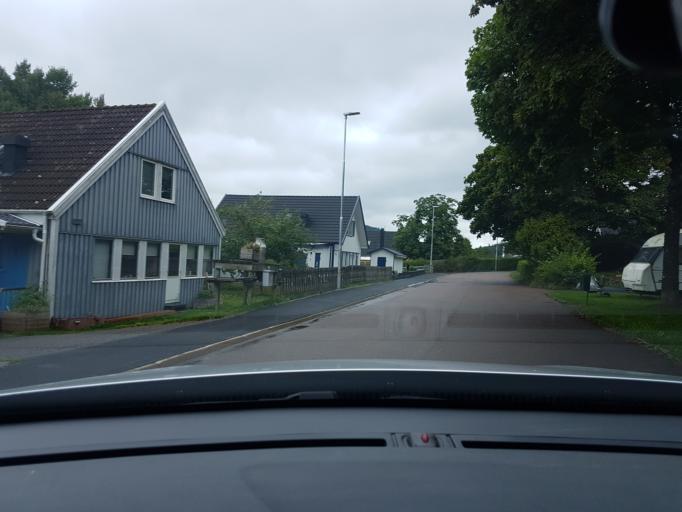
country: SE
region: Vaestra Goetaland
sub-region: Ale Kommun
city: Salanda
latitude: 57.9815
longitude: 12.2165
